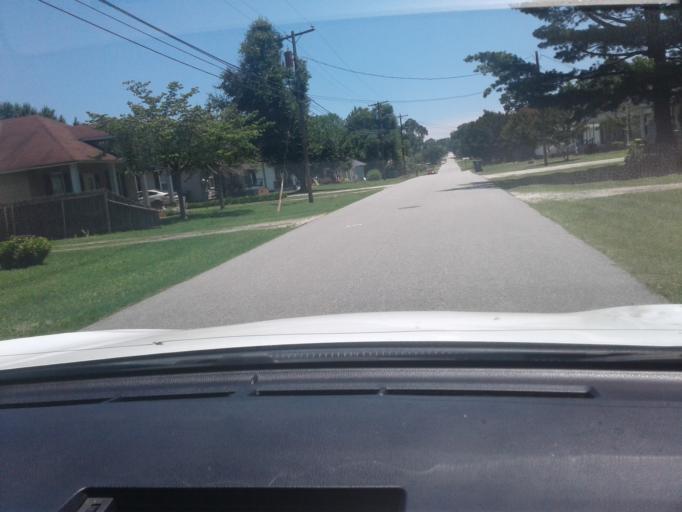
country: US
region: North Carolina
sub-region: Harnett County
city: Erwin
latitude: 35.3249
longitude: -78.6824
